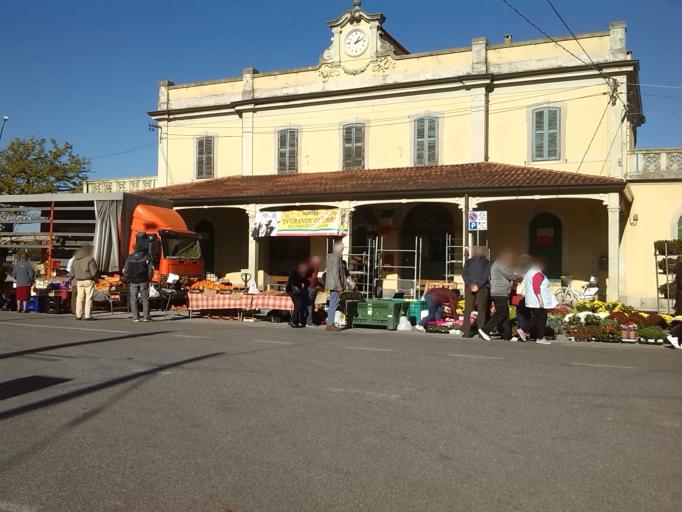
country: IT
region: Friuli Venezia Giulia
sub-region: Provincia di Udine
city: Cividale del Friuli
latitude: 46.0951
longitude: 13.4256
